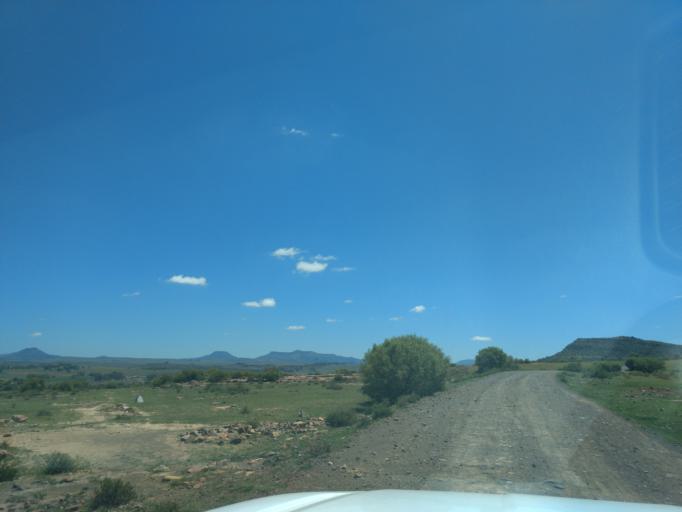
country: LS
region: Maseru
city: Maseru
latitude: -29.4579
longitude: 27.3682
